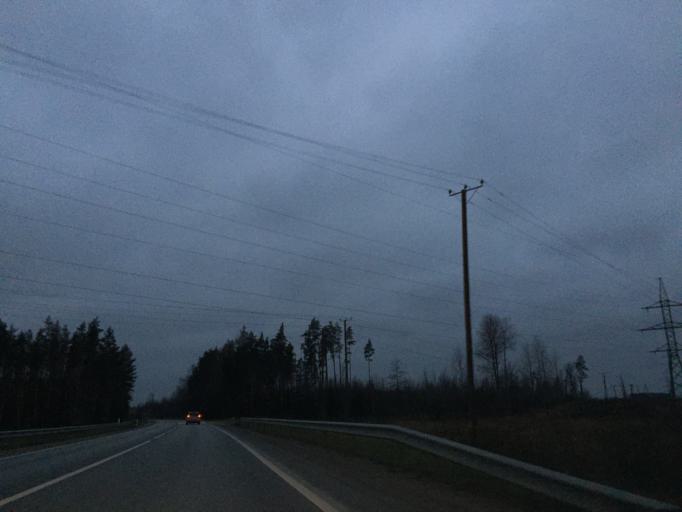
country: LV
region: Koceni
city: Koceni
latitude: 57.5405
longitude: 25.3751
